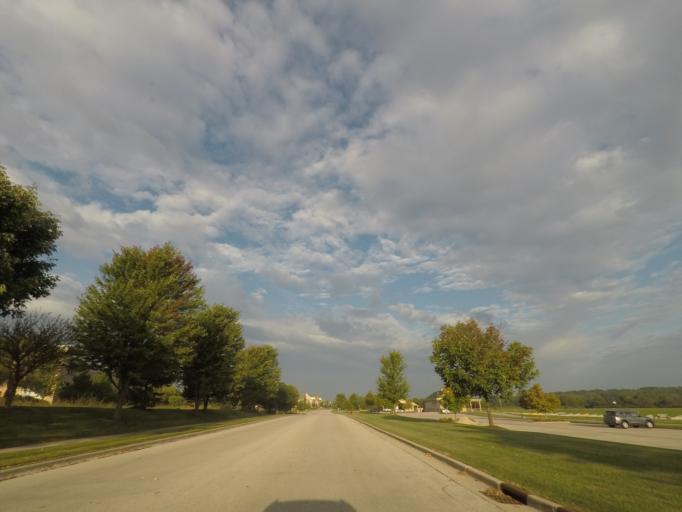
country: US
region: Wisconsin
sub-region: Waukesha County
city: Brookfield
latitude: 43.0392
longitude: -88.1119
